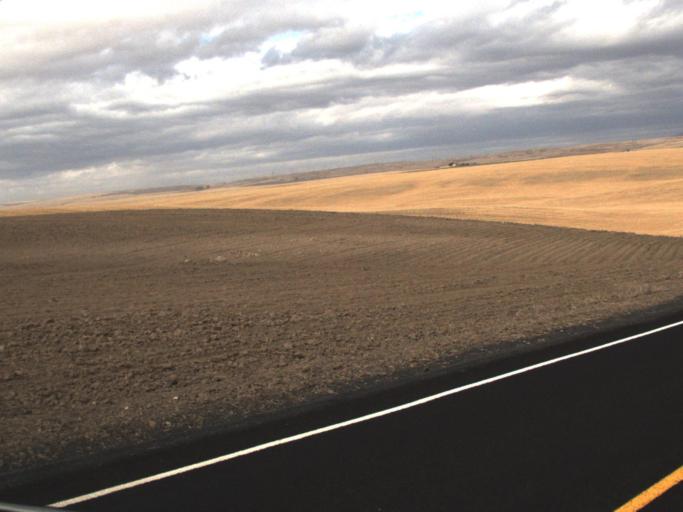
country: US
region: Washington
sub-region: Okanogan County
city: Coulee Dam
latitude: 47.8016
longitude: -118.7218
